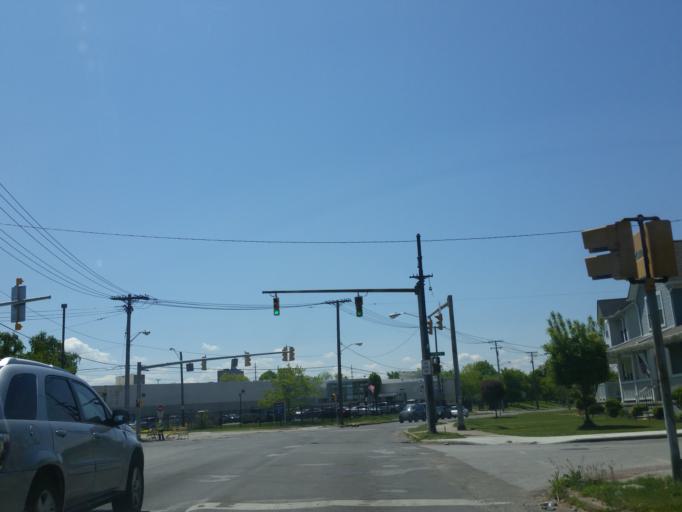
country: US
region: Ohio
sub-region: Cuyahoga County
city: East Cleveland
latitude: 41.5339
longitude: -81.5867
